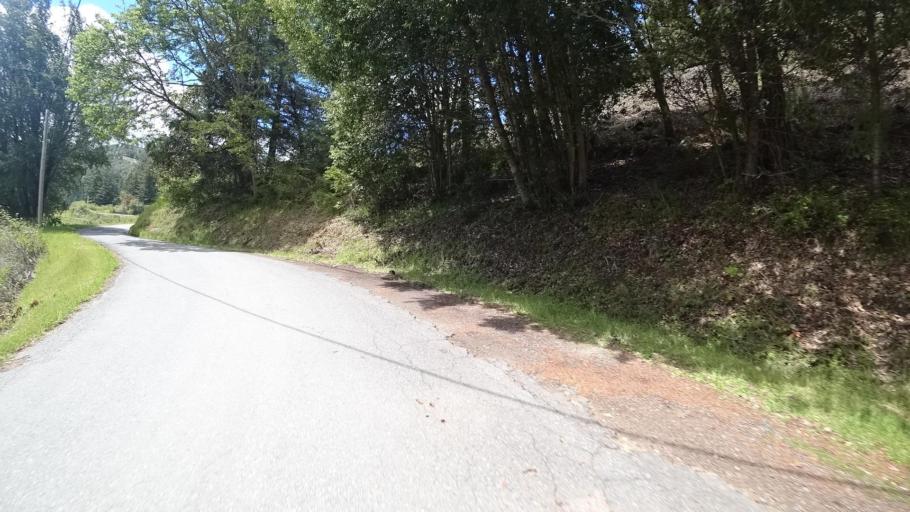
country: US
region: California
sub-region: Humboldt County
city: Blue Lake
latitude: 40.7663
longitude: -123.9387
